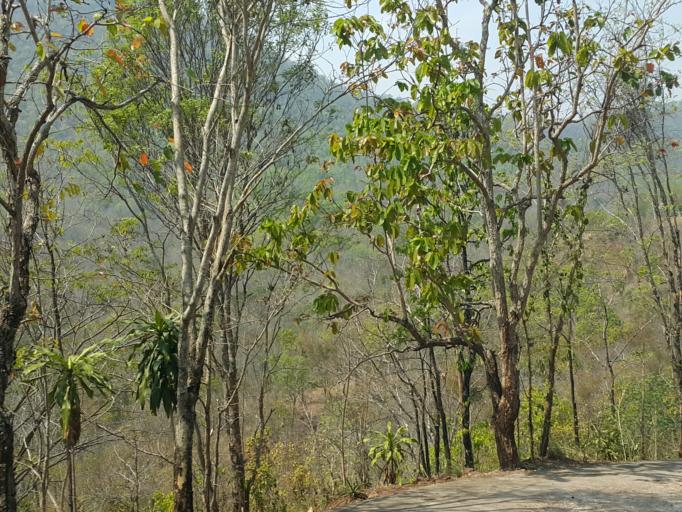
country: TH
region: Lampang
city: Chae Hom
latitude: 18.7424
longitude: 99.5430
